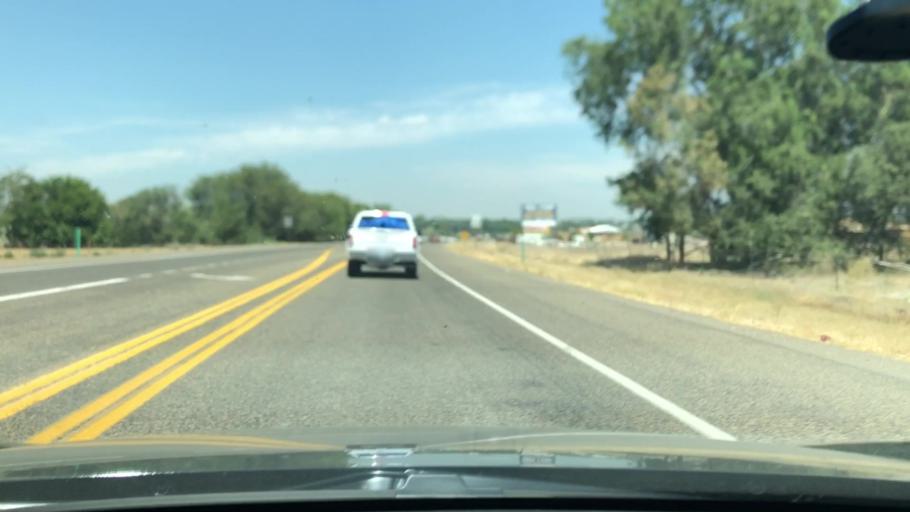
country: US
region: Idaho
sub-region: Owyhee County
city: Homedale
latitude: 43.6102
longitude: -116.9302
